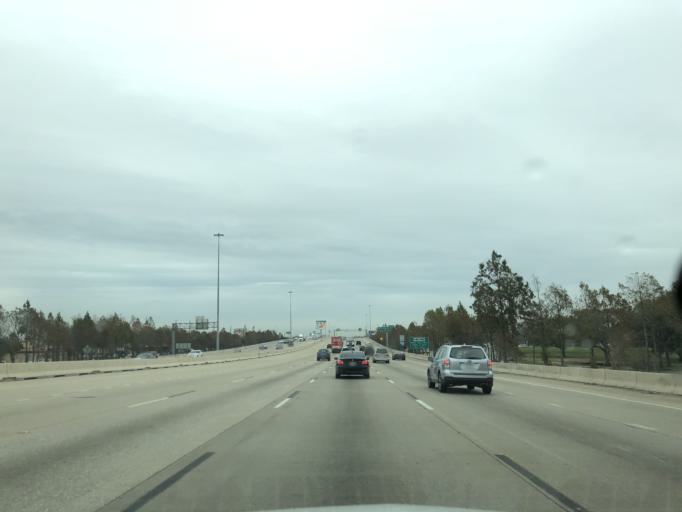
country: US
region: Texas
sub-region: Fort Bend County
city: Meadows Place
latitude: 29.6403
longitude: -95.5800
